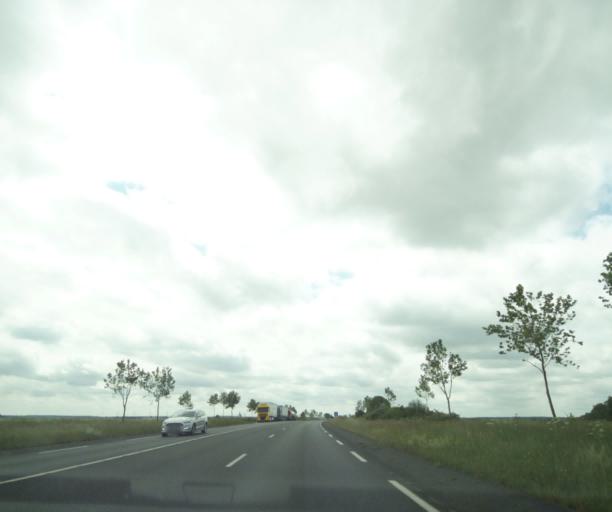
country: FR
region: Poitou-Charentes
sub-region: Departement des Deux-Sevres
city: Saint-Varent
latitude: 46.9074
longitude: -0.1920
